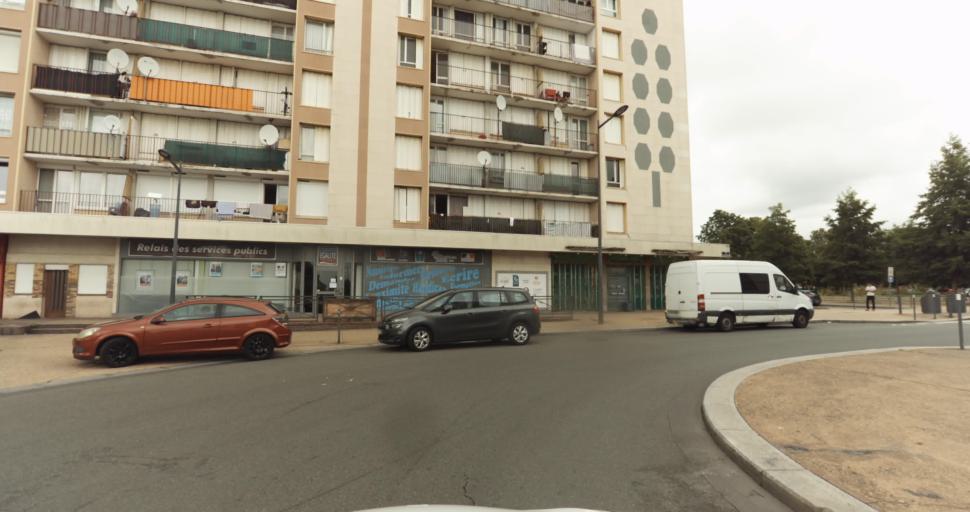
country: FR
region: Haute-Normandie
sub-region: Departement de l'Eure
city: Evreux
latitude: 49.0095
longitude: 1.1607
